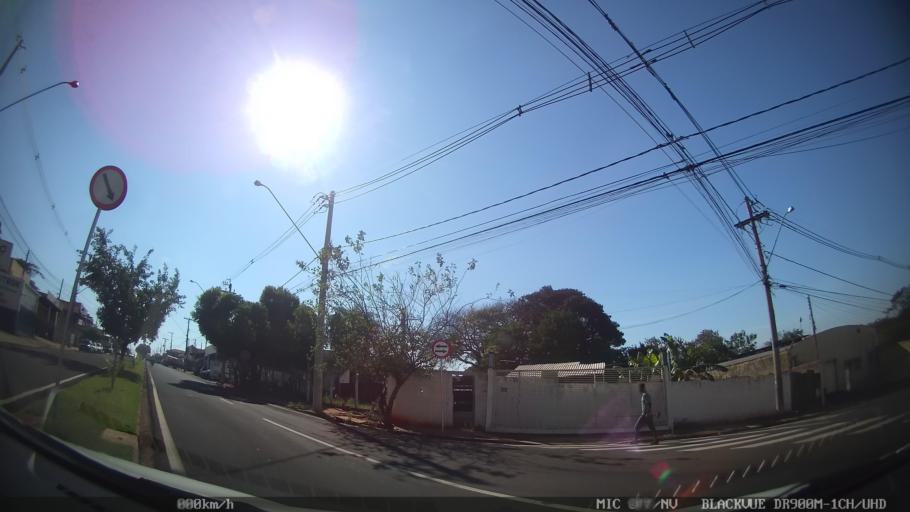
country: BR
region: Sao Paulo
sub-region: Sao Jose Do Rio Preto
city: Sao Jose do Rio Preto
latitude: -20.7873
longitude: -49.3884
